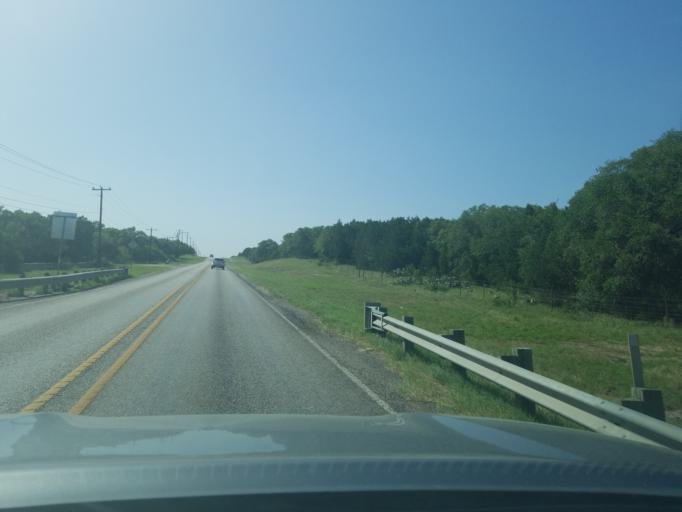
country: US
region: Texas
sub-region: Comal County
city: Garden Ridge
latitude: 29.6824
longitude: -98.3253
